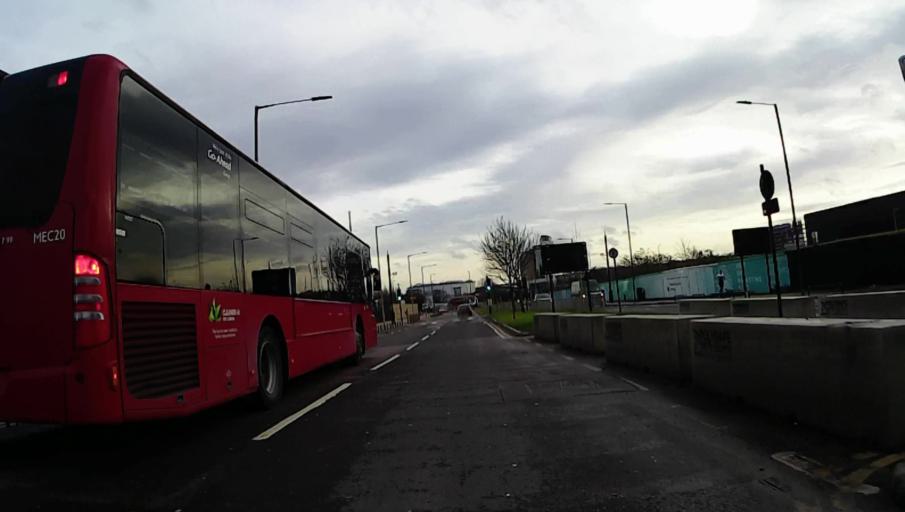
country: GB
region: England
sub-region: Greater London
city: Poplar
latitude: 51.4950
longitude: 0.0082
